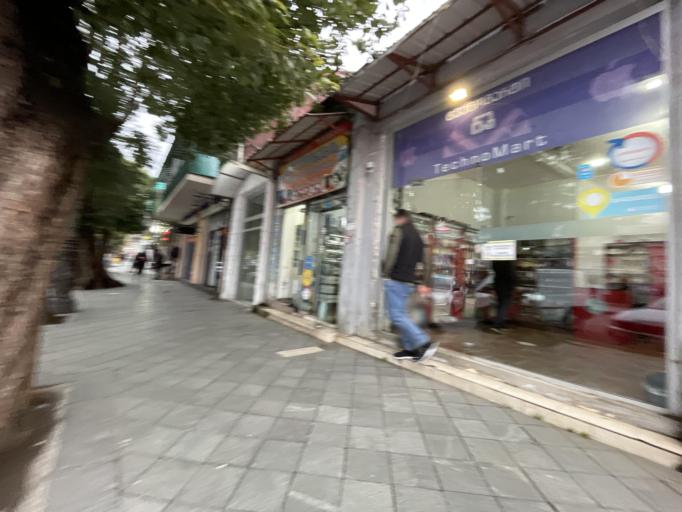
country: GE
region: Ajaria
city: Batumi
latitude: 41.6466
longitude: 41.6413
